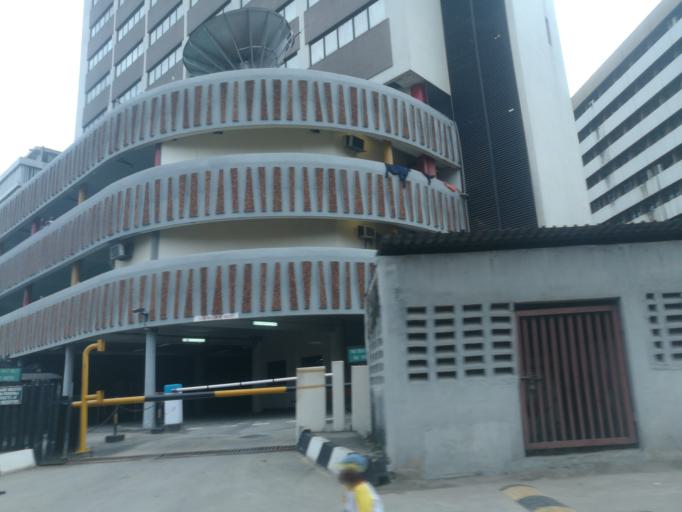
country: NG
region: Lagos
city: Lagos
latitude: 6.4499
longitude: 3.3937
